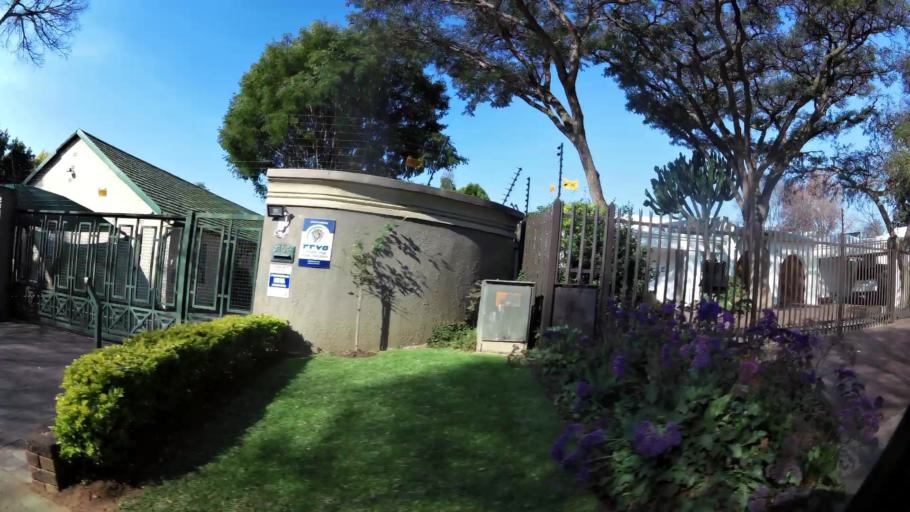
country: ZA
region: Gauteng
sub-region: City of Johannesburg Metropolitan Municipality
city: Roodepoort
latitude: -26.1071
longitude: 27.9573
